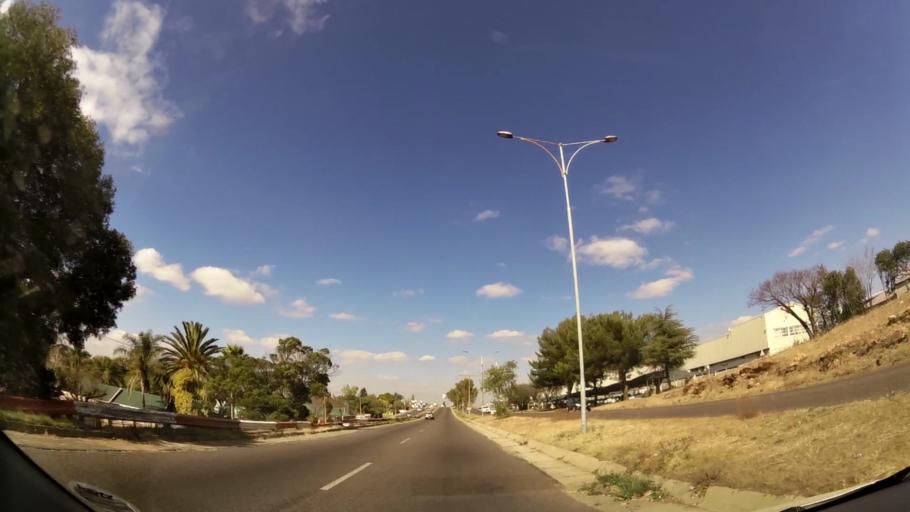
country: ZA
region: Gauteng
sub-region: West Rand District Municipality
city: Krugersdorp
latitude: -26.1152
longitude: 27.8163
